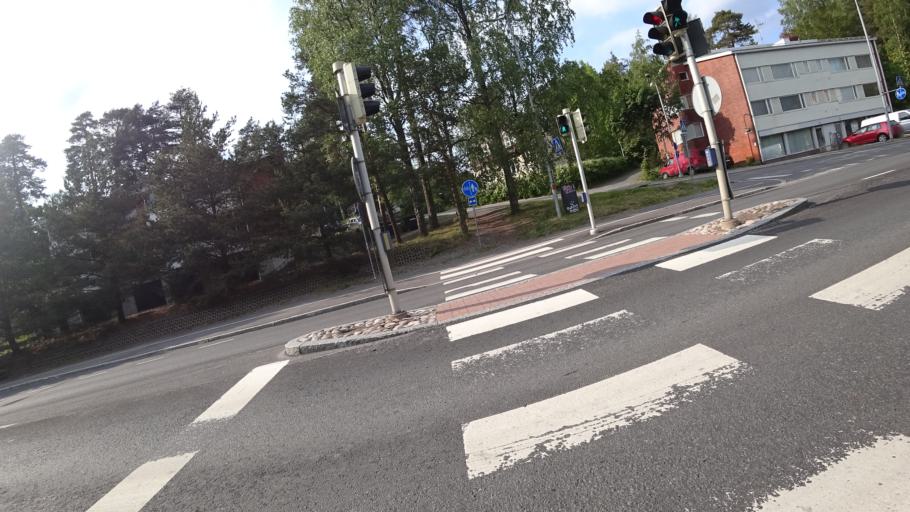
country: FI
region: Pirkanmaa
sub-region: Tampere
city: Pirkkala
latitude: 61.4990
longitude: 23.6369
